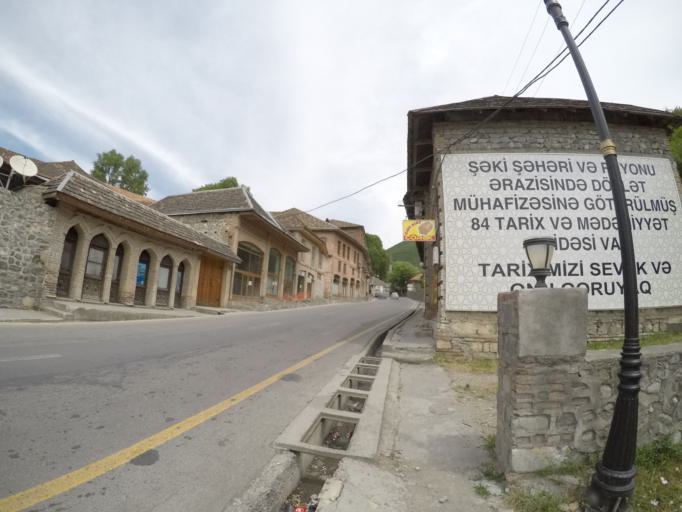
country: AZ
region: Shaki City
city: Sheki
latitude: 41.2002
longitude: 47.1898
